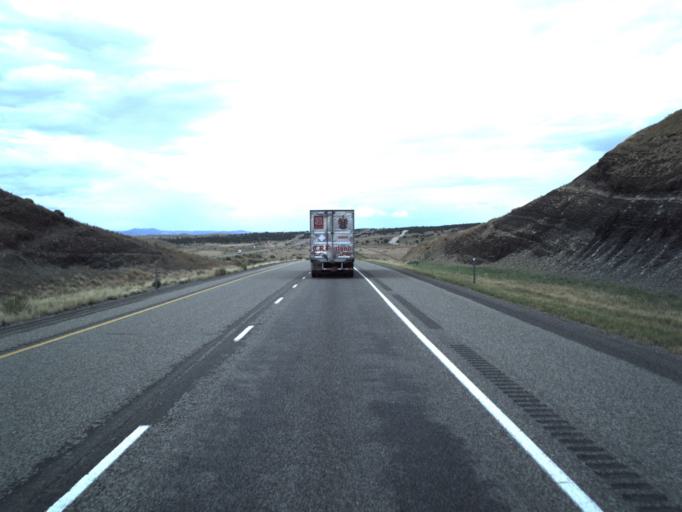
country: US
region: Colorado
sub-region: Mesa County
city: Loma
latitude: 39.1433
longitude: -109.1528
